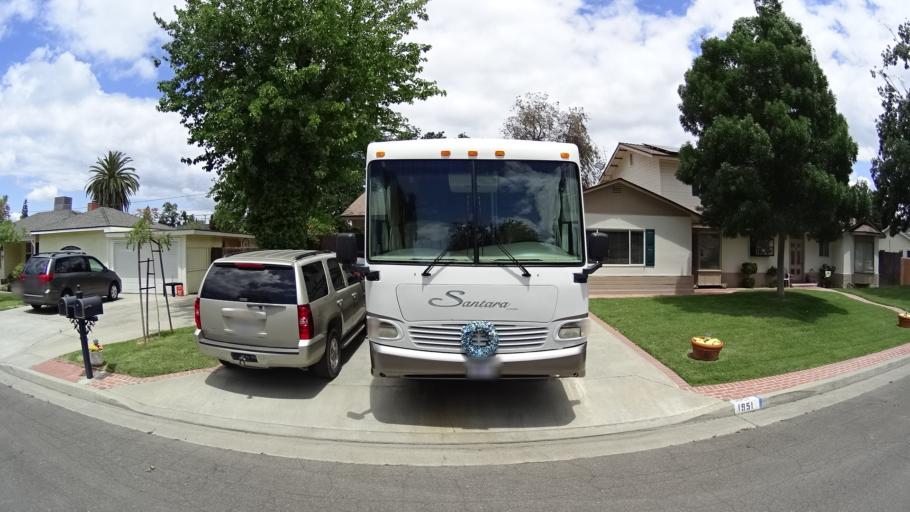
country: US
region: California
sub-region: Kings County
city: Hanford
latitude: 36.3487
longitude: -119.6526
